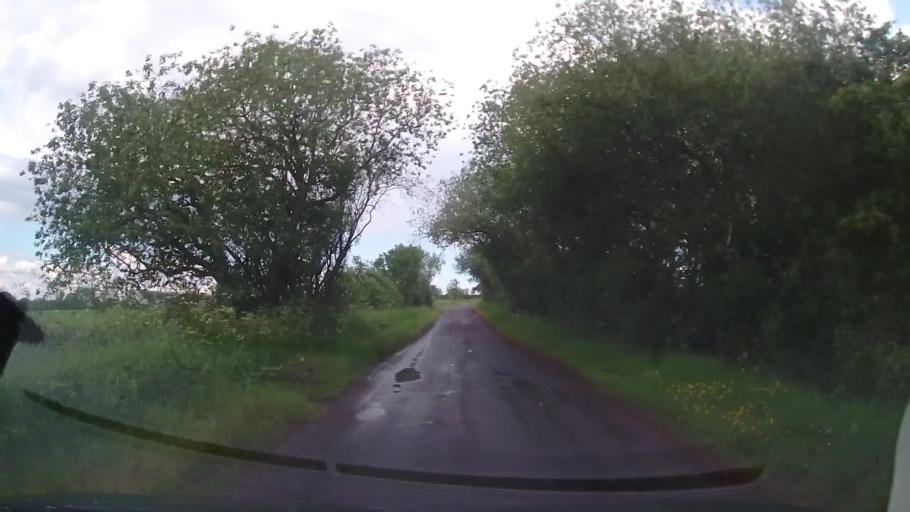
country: GB
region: England
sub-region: Telford and Wrekin
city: Ironbridge
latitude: 52.6565
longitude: -2.5174
